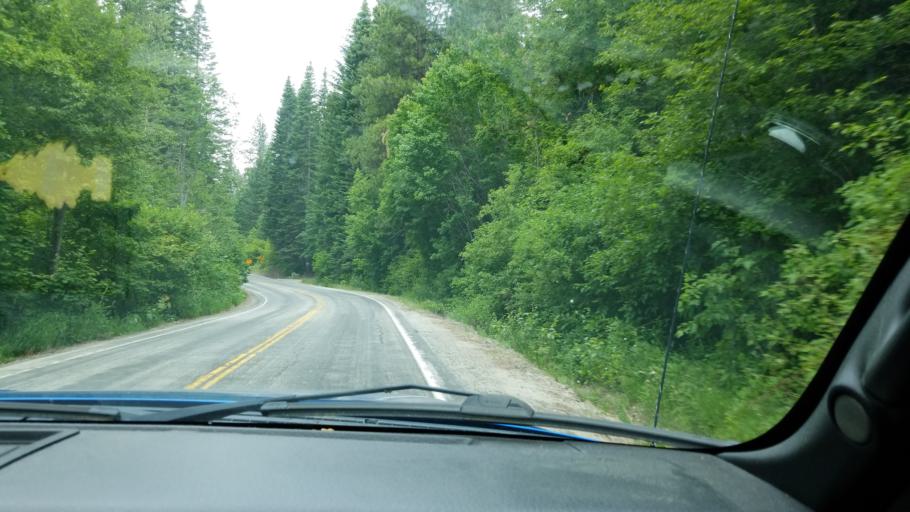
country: US
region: Washington
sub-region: Chelan County
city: Leavenworth
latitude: 47.8481
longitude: -120.8283
